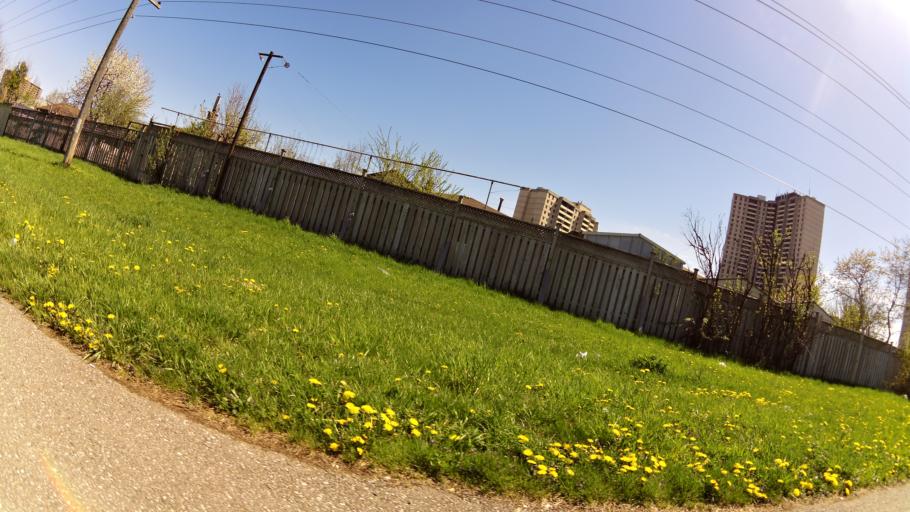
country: CA
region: Ontario
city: Concord
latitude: 43.7606
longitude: -79.5157
